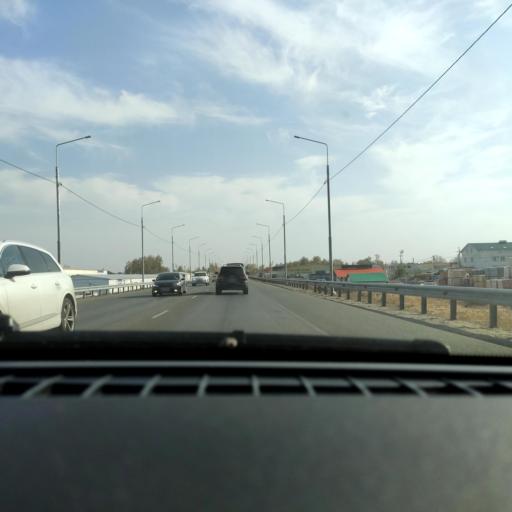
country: RU
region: Voronezj
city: Somovo
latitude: 51.6775
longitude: 39.3135
